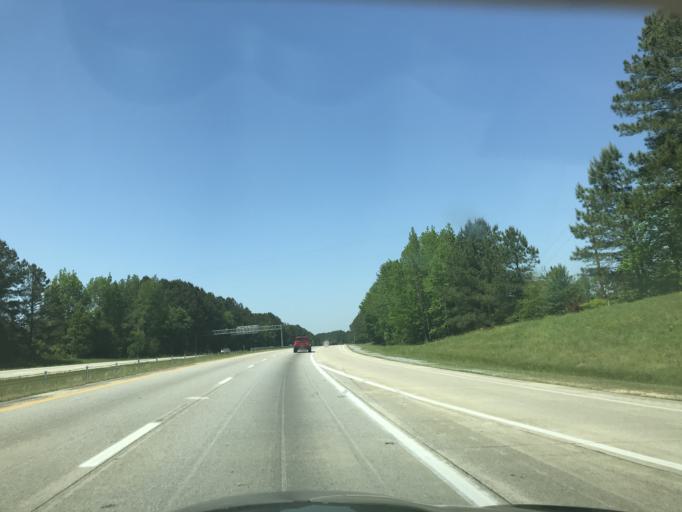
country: US
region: North Carolina
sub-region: Johnston County
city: Benson
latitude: 35.4413
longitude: -78.5344
